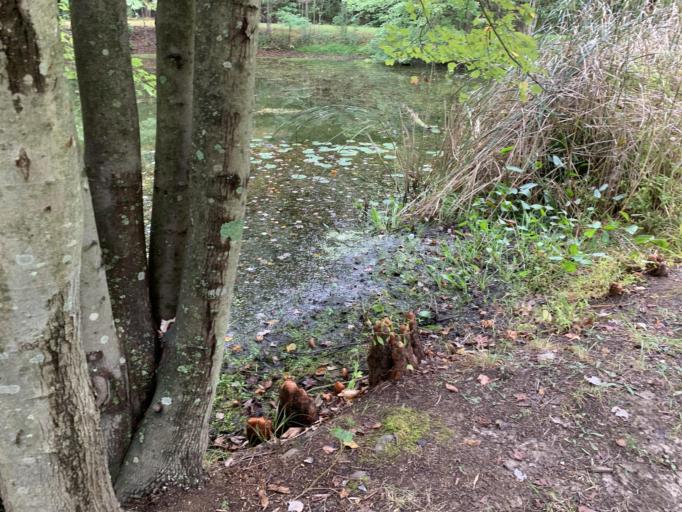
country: US
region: Delaware
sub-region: New Castle County
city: Townsend
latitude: 39.3458
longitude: -75.6736
